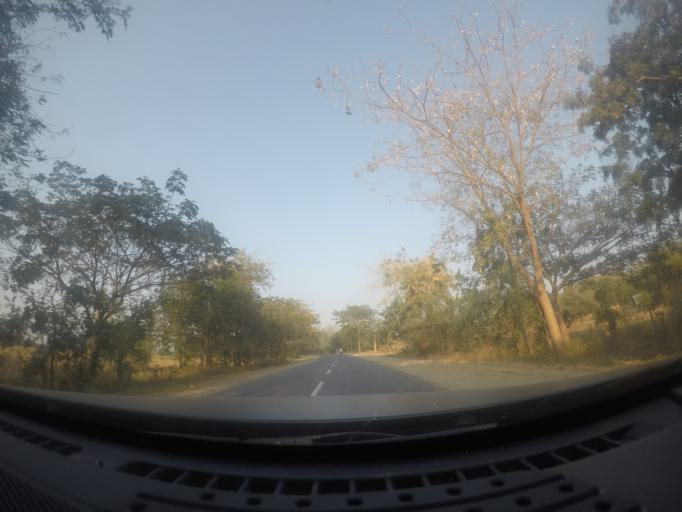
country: MM
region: Mandalay
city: Yamethin
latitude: 20.7300
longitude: 96.2027
